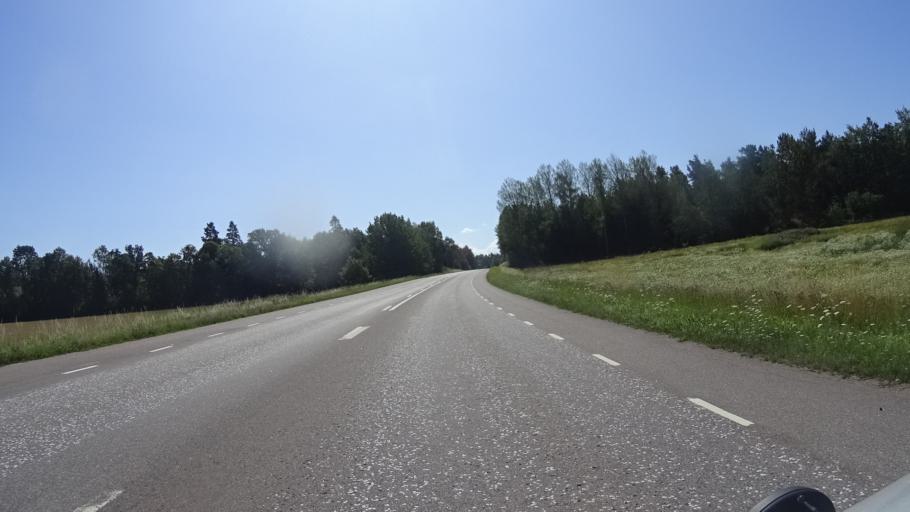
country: SE
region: OEstergoetland
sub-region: Vadstena Kommun
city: Herrestad
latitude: 58.3095
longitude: 14.9090
